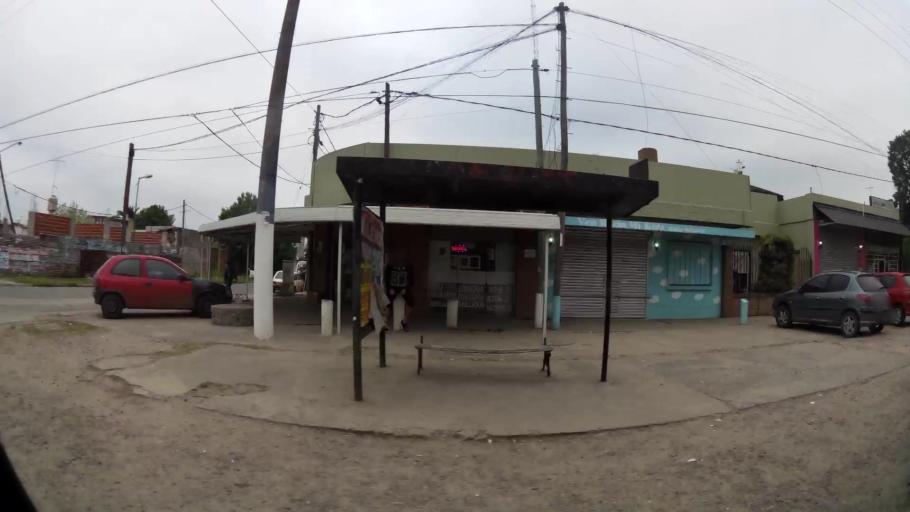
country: AR
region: Buenos Aires
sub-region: Partido de La Plata
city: La Plata
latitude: -34.9310
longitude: -58.0023
